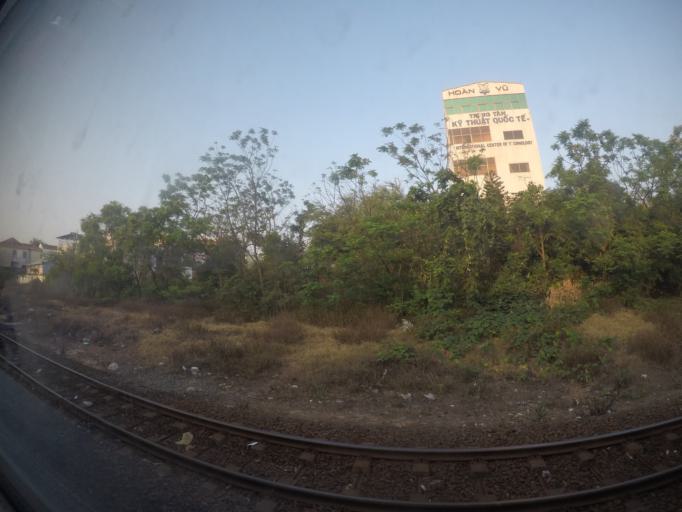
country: VN
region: Phu Yen
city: Tuy Hoa
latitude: 13.0883
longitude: 109.2967
